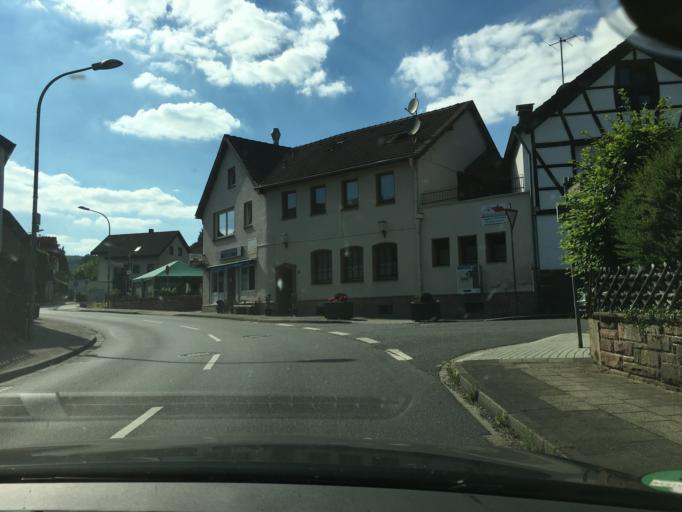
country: DE
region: North Rhine-Westphalia
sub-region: Regierungsbezirk Koln
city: Kreuzau
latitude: 50.7284
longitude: 6.4557
